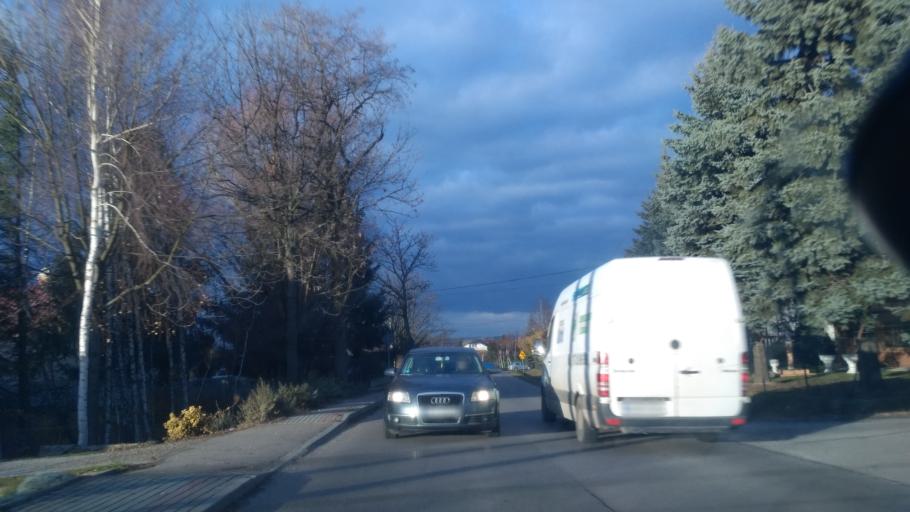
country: PL
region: Subcarpathian Voivodeship
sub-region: Powiat rzeszowski
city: Krasne
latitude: 50.0534
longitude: 22.1219
